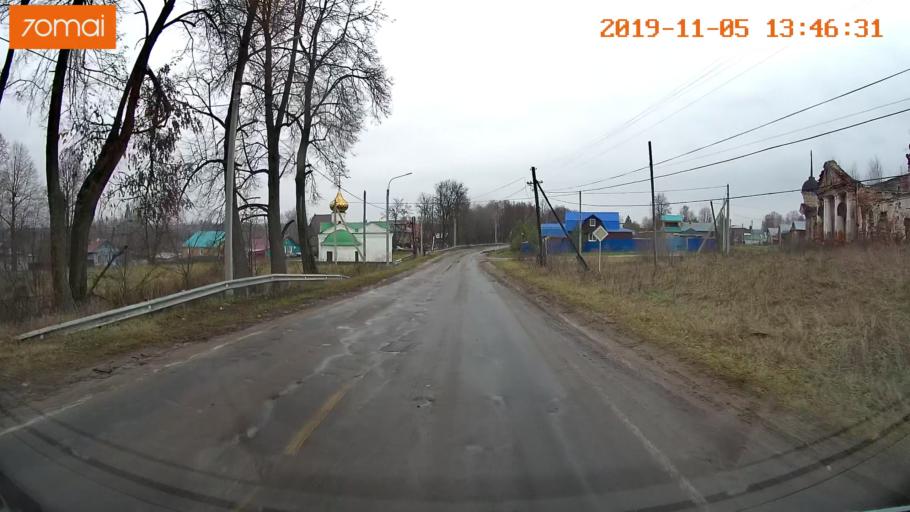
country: RU
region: Ivanovo
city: Shuya
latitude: 56.9957
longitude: 41.4099
